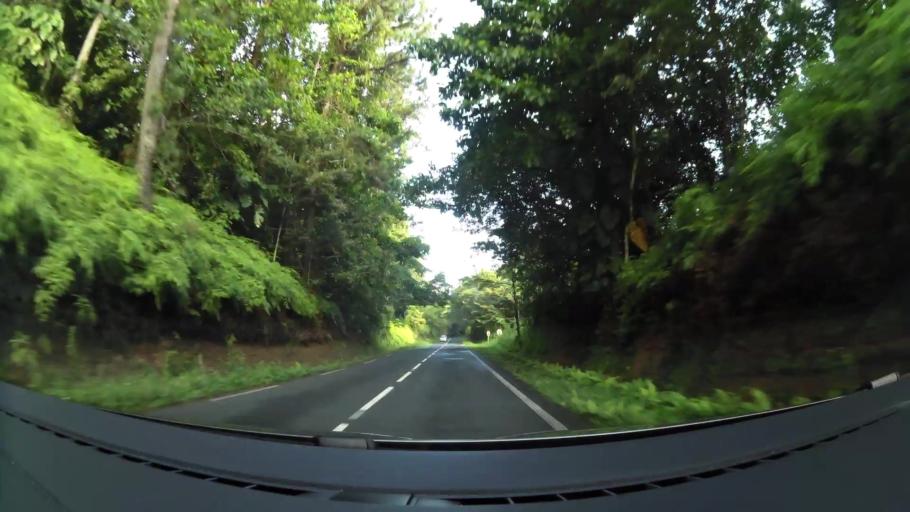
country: GP
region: Guadeloupe
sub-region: Guadeloupe
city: Bouillante
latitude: 16.1786
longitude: -61.7067
